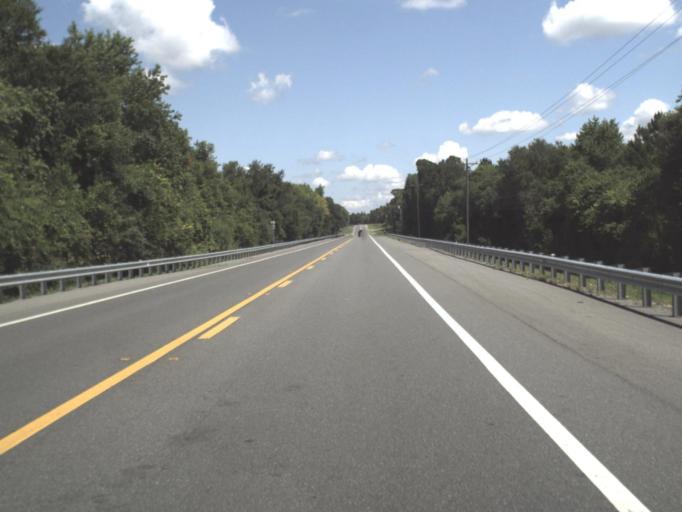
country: US
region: Florida
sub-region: Clay County
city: Keystone Heights
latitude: 29.7492
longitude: -81.9938
